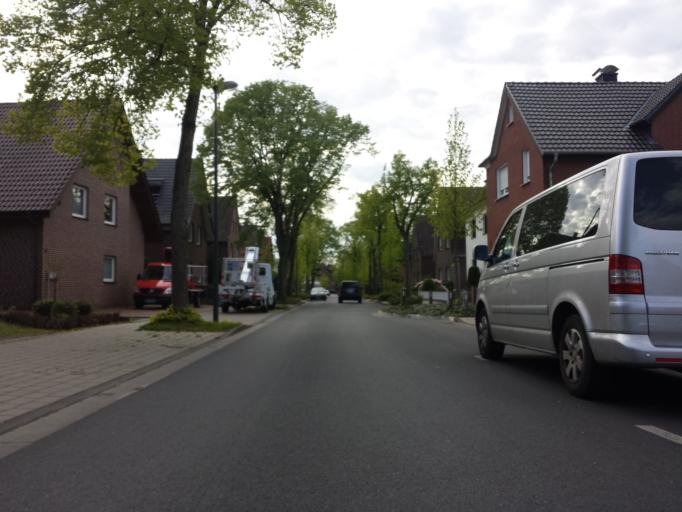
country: DE
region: North Rhine-Westphalia
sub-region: Regierungsbezirk Detmold
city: Guetersloh
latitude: 51.8925
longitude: 8.3705
